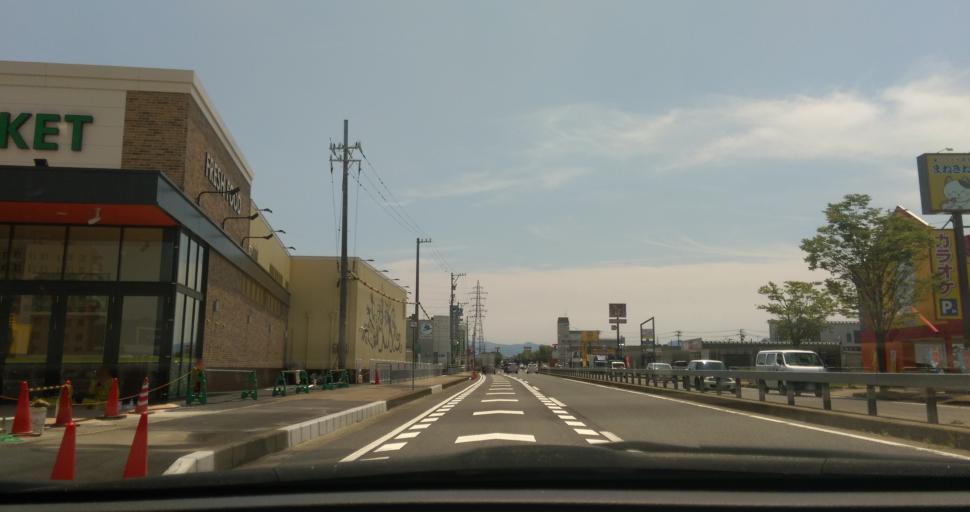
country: JP
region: Fukui
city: Sabae
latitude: 35.9413
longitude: 136.1929
